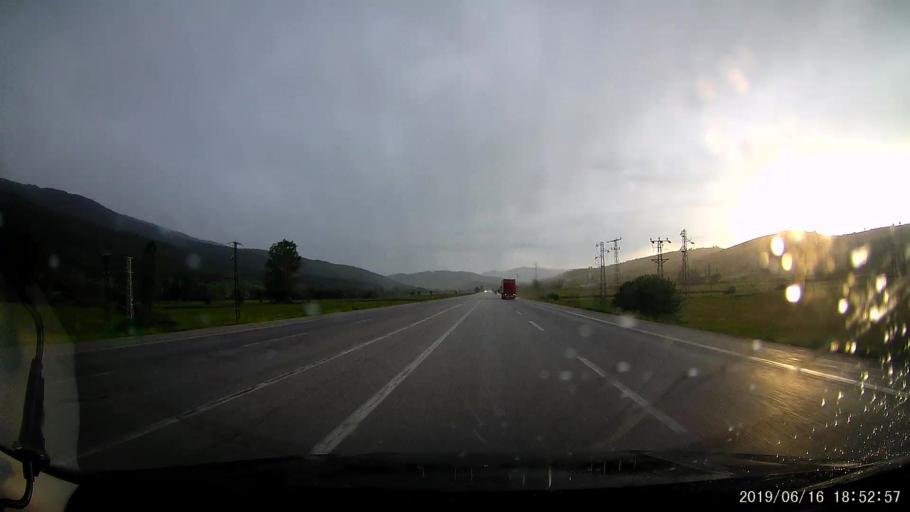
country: TR
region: Erzincan
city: Catalcam
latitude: 39.9005
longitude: 38.8891
